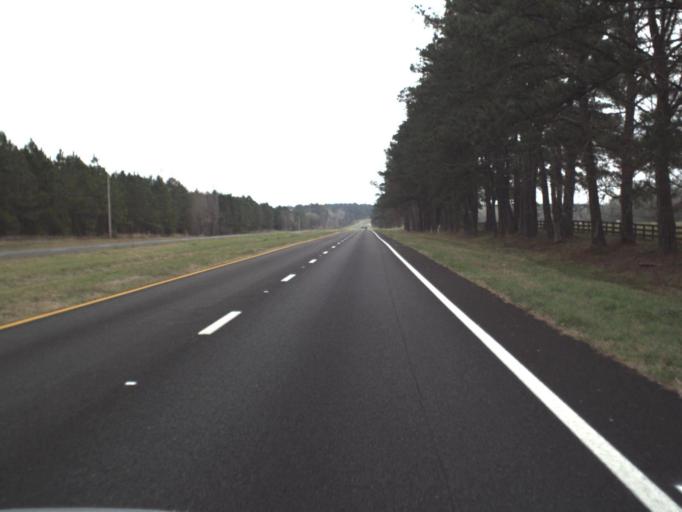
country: US
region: Florida
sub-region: Jefferson County
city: Monticello
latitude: 30.3883
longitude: -83.8515
